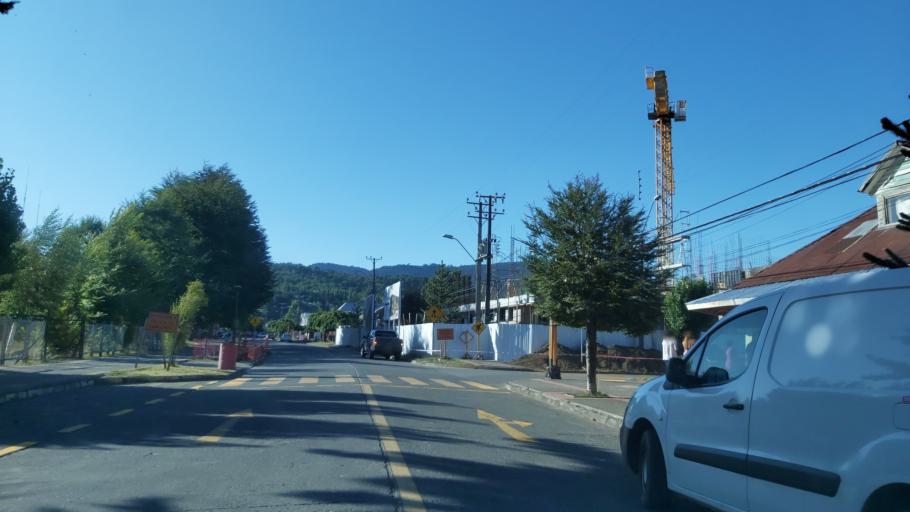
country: AR
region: Neuquen
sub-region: Departamento de Loncopue
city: Loncopue
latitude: -38.4532
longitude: -71.3703
